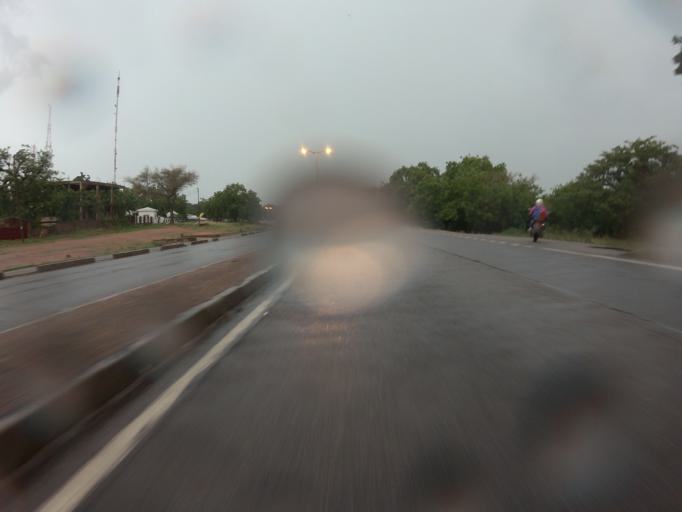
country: GH
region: Upper East
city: Bolgatanga
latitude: 10.8005
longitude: -0.8609
